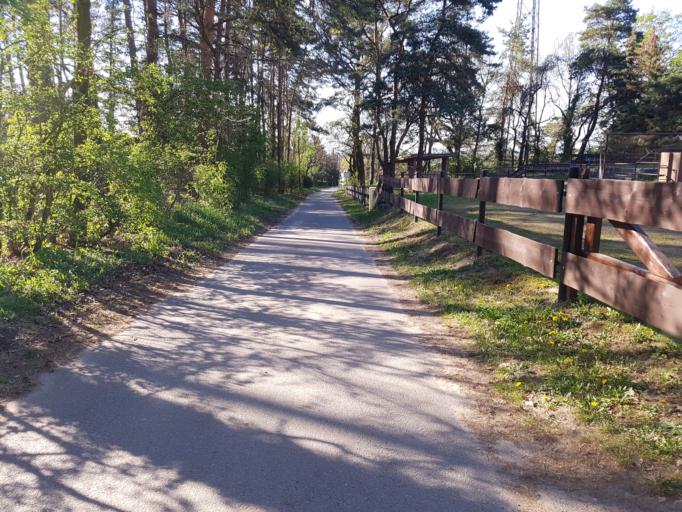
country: DE
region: Brandenburg
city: Groden
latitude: 51.4010
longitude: 13.5727
